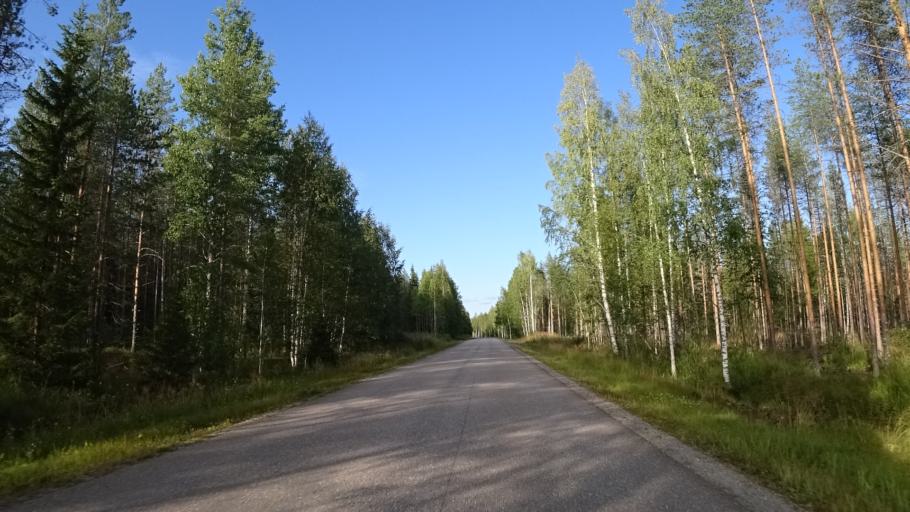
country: FI
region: North Karelia
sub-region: Joensuu
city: Eno
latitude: 63.0137
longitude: 30.4837
